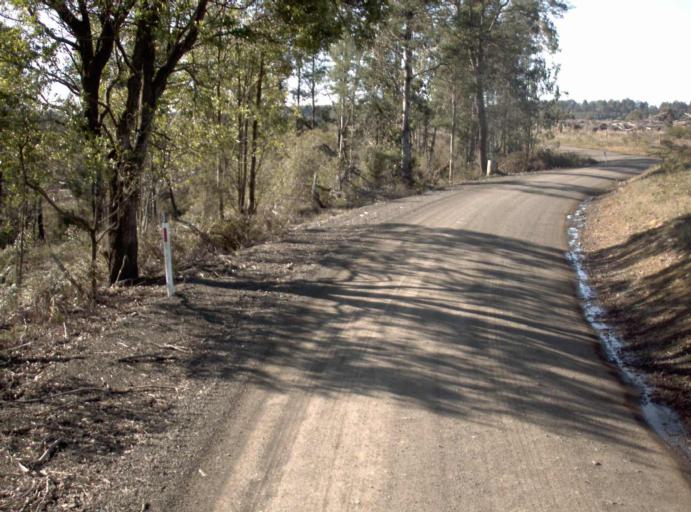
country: AU
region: Tasmania
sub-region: Launceston
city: Mayfield
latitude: -41.2143
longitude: 147.1774
